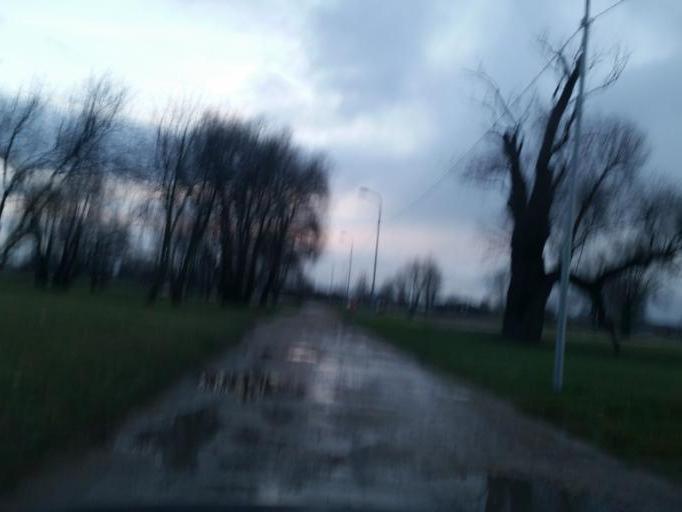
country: LV
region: Riga
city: Riga
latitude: 56.9276
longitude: 24.1161
